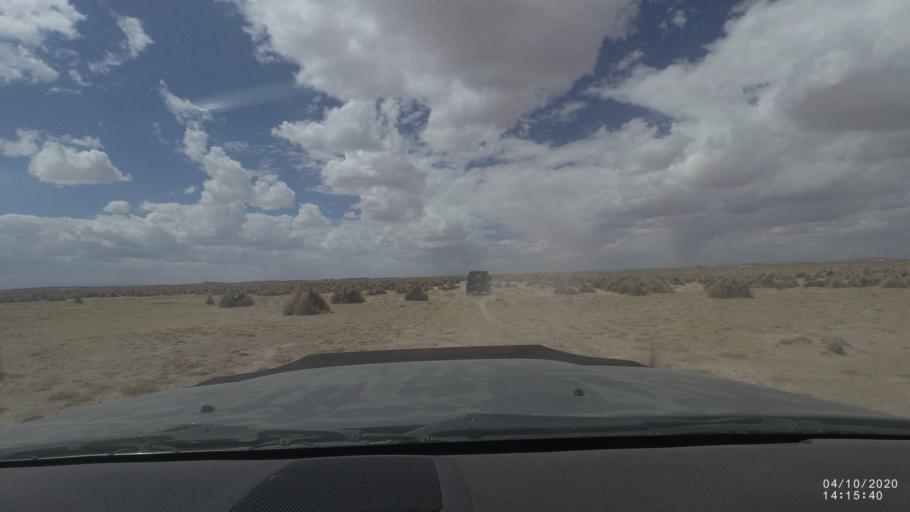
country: BO
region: Oruro
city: Poopo
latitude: -18.6925
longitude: -67.4536
